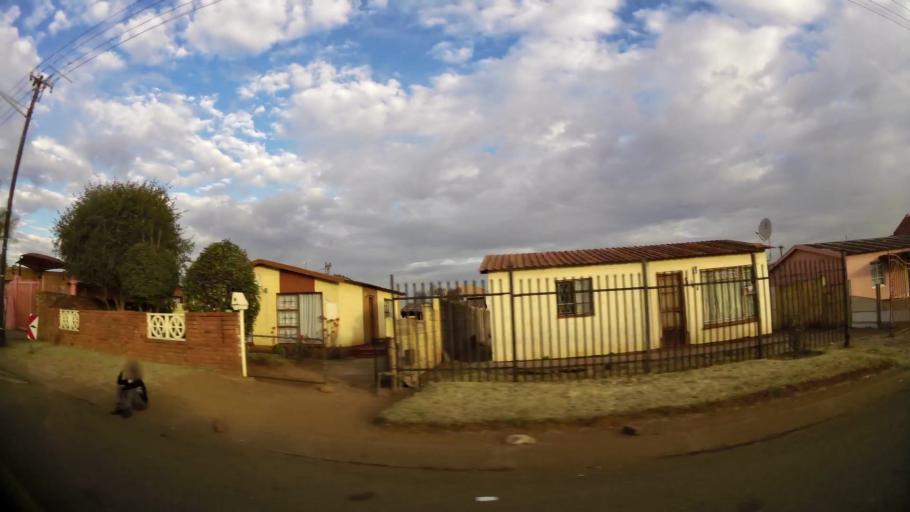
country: ZA
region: Gauteng
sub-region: City of Tshwane Metropolitan Municipality
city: Pretoria
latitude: -25.7053
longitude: 28.3223
